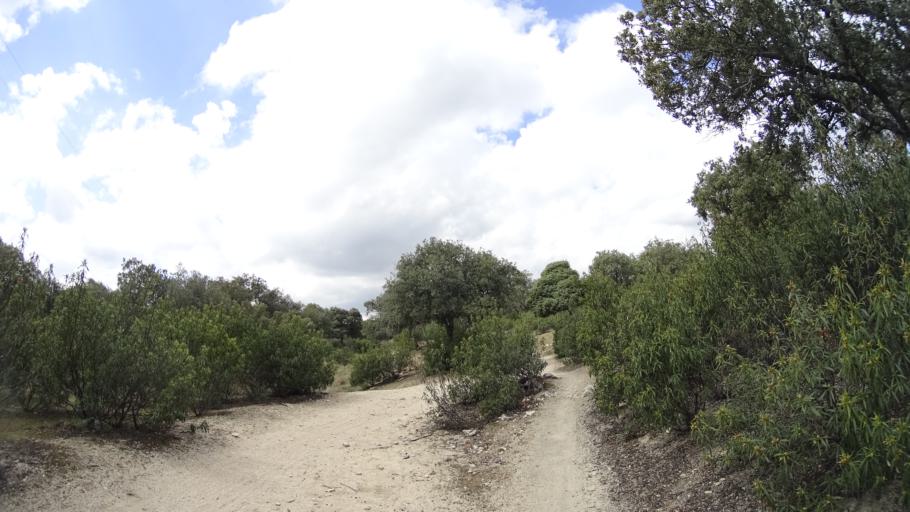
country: ES
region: Madrid
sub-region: Provincia de Madrid
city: Hoyo de Manzanares
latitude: 40.6202
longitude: -3.8879
